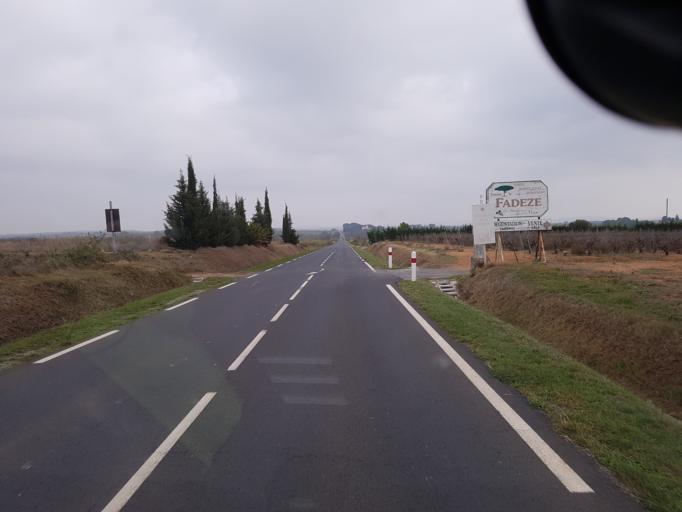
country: FR
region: Languedoc-Roussillon
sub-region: Departement de l'Herault
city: Marseillan
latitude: 43.3767
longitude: 3.5342
